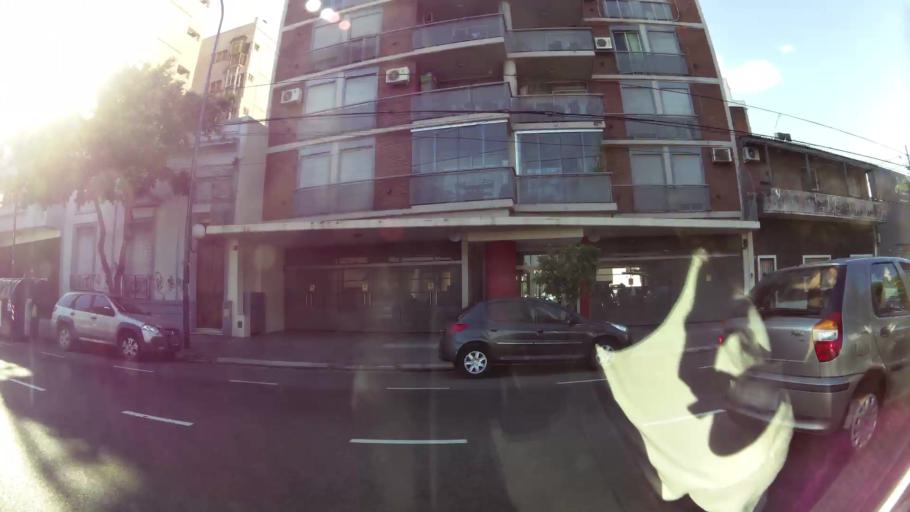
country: AR
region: Buenos Aires F.D.
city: Villa Santa Rita
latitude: -34.6185
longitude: -58.4493
